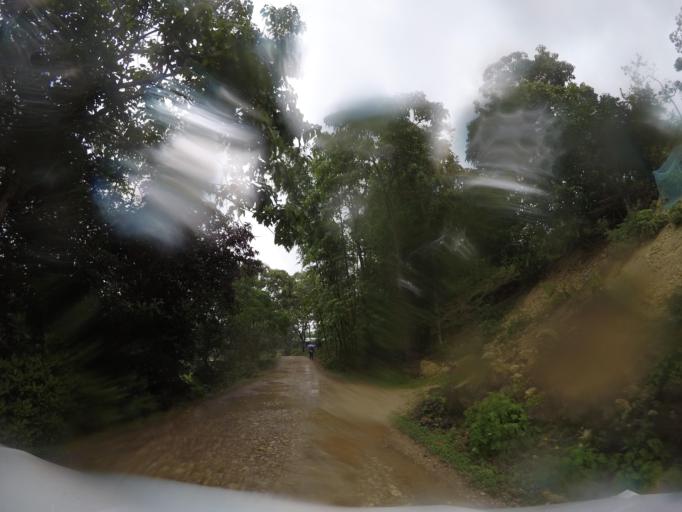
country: TL
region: Baucau
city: Venilale
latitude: -8.6420
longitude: 126.3954
